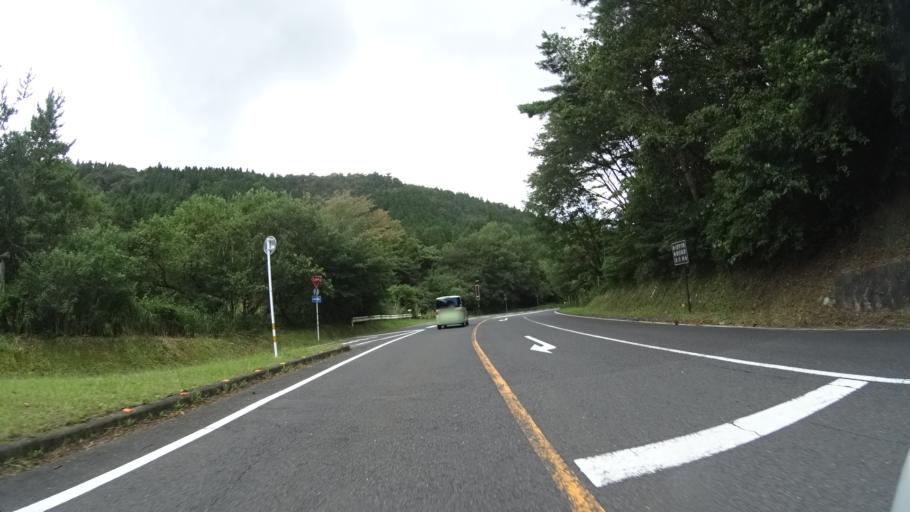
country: JP
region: Oita
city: Tsukawaki
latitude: 33.1896
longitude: 131.2820
